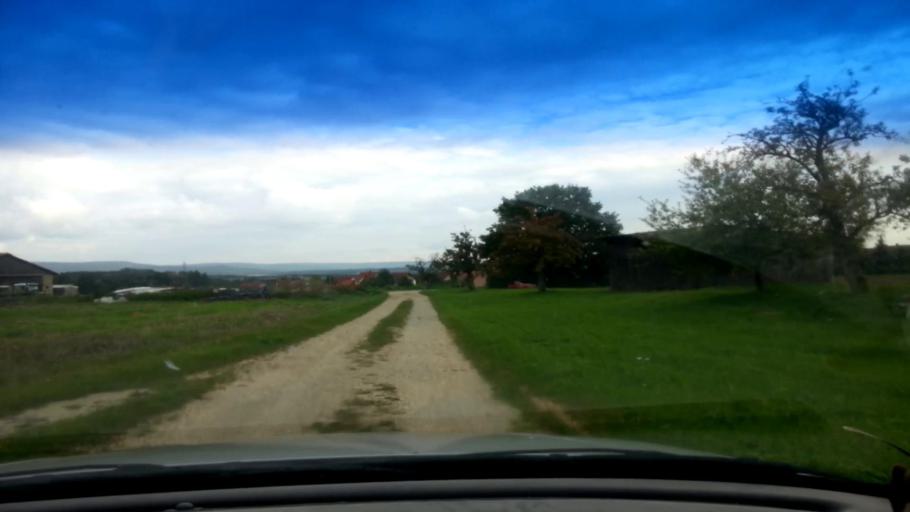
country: DE
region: Bavaria
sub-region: Upper Franconia
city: Memmelsdorf
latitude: 49.9626
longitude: 10.9570
